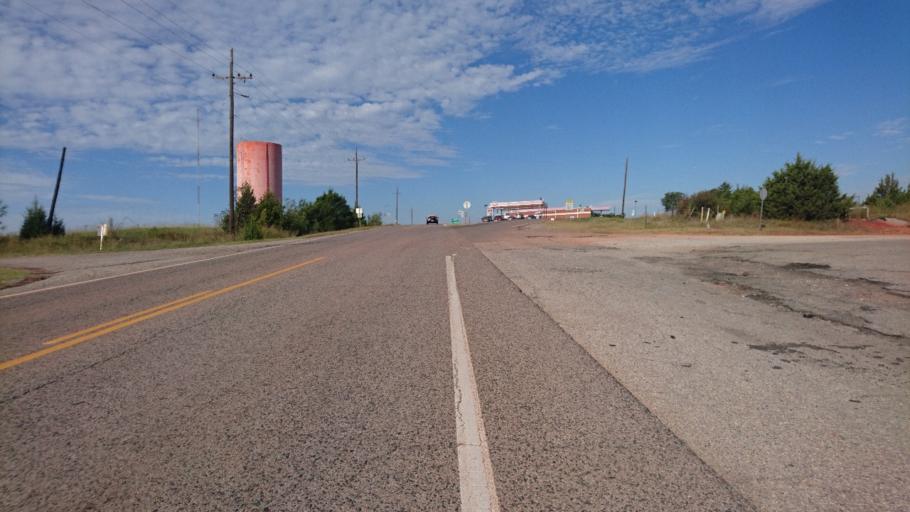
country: US
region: Oklahoma
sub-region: Oklahoma County
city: Luther
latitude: 35.6811
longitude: -97.0523
